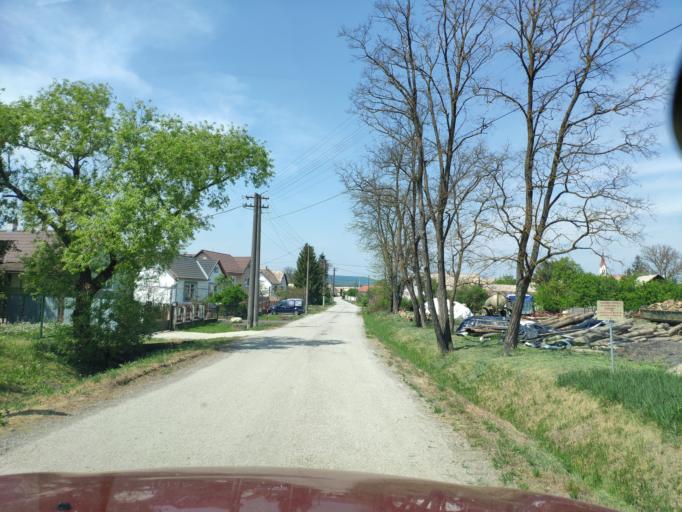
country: SK
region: Banskobystricky
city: Rimavska Sobota
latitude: 48.4158
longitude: 20.1477
